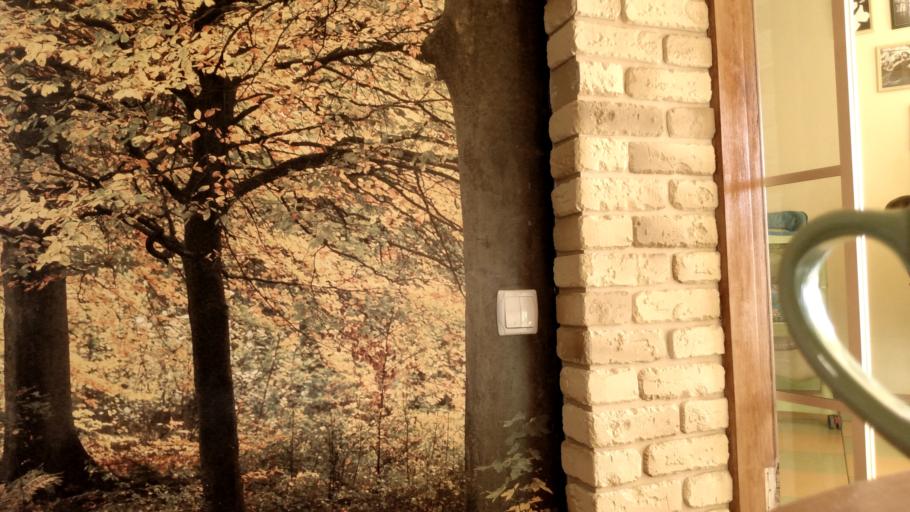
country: RU
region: Vologda
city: Imeni Zhelyabova
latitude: 58.8124
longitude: 36.8827
